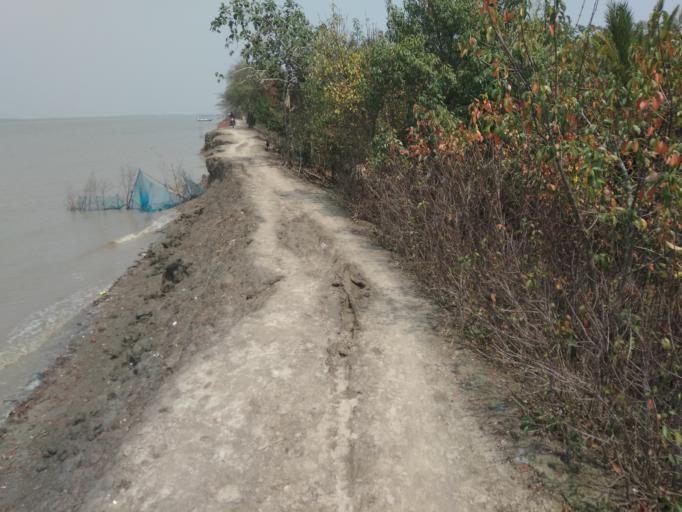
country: IN
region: West Bengal
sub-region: North 24 Parganas
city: Gosaba
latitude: 22.2496
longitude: 89.2501
